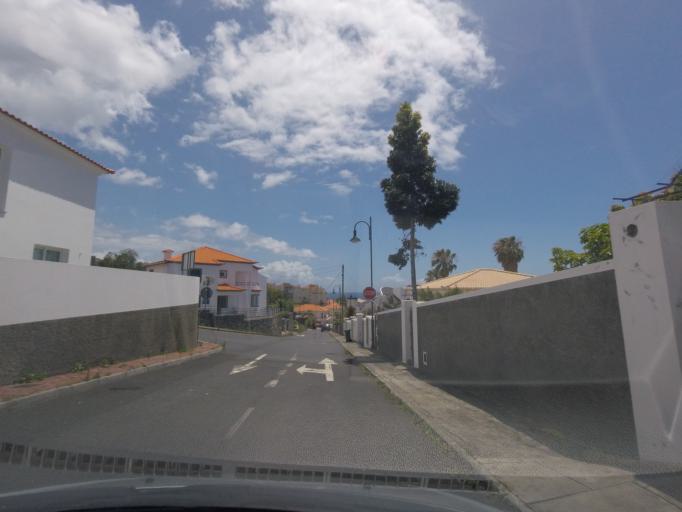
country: PT
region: Madeira
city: Canico
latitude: 32.6436
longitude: -16.8377
